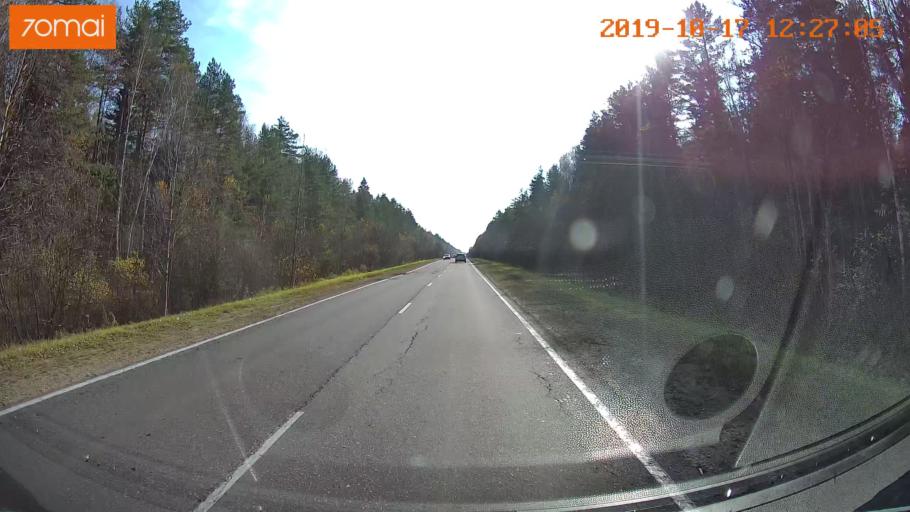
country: RU
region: Rjazan
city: Syntul
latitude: 55.0100
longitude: 41.2603
